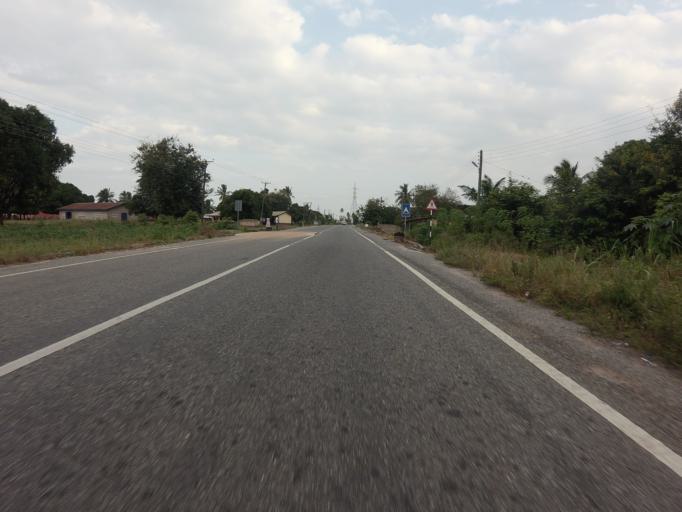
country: GH
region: Volta
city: Ho
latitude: 6.2627
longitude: 0.5479
